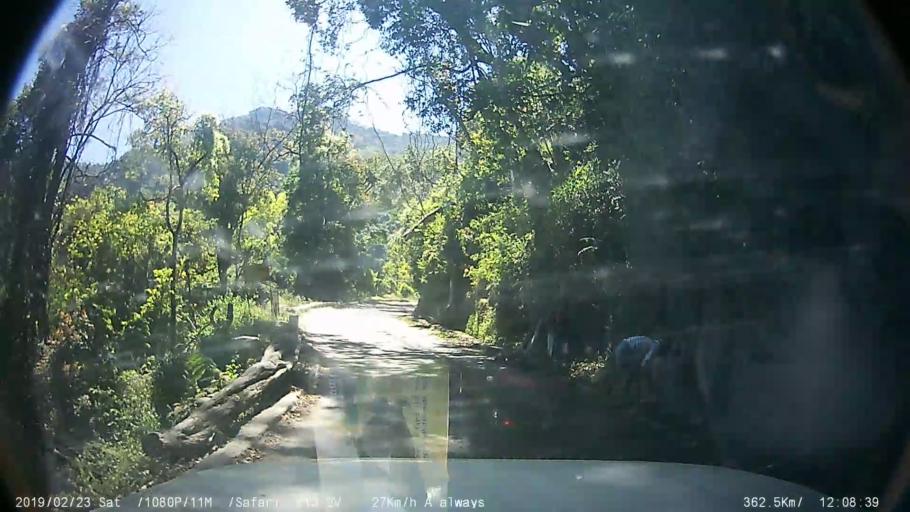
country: IN
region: Tamil Nadu
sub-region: Nilgiri
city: Wellington
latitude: 11.3326
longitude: 76.8087
